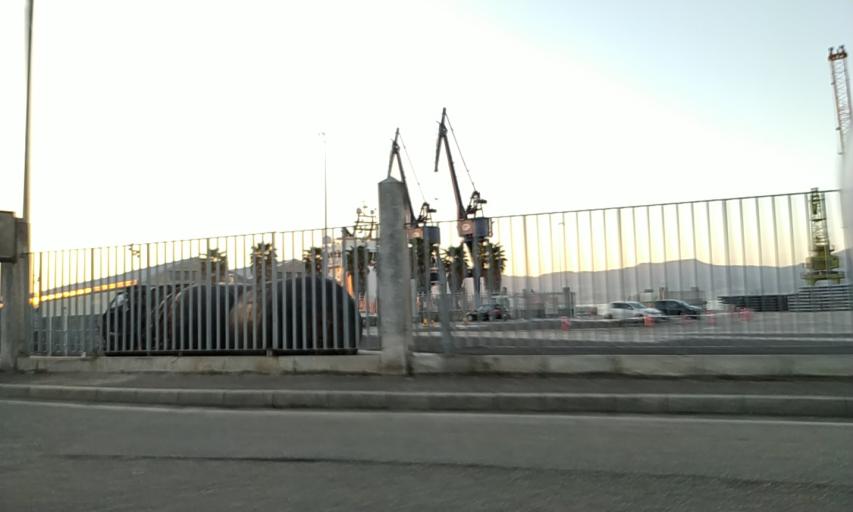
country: ES
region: Galicia
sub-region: Provincia de Pontevedra
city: Vigo
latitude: 42.2402
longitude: -8.7174
